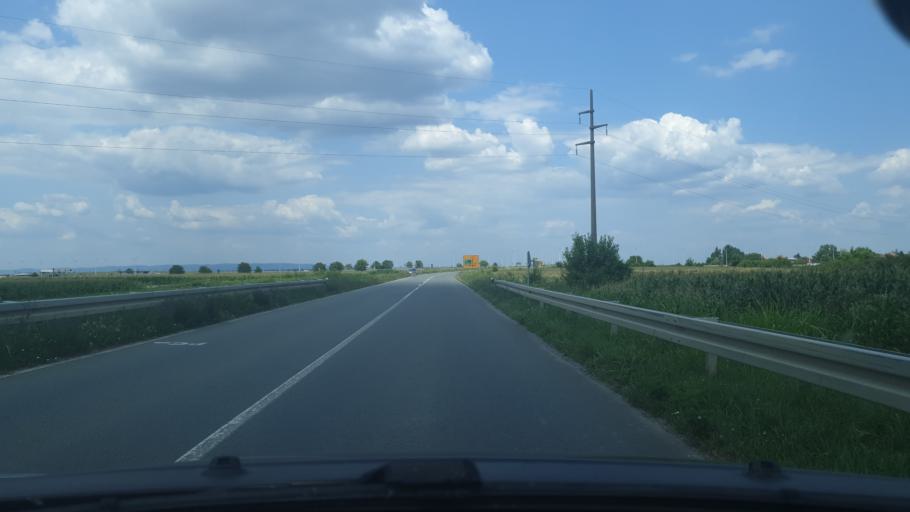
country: RS
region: Autonomna Pokrajina Vojvodina
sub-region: Sremski Okrug
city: Pecinci
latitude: 44.9138
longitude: 19.9566
